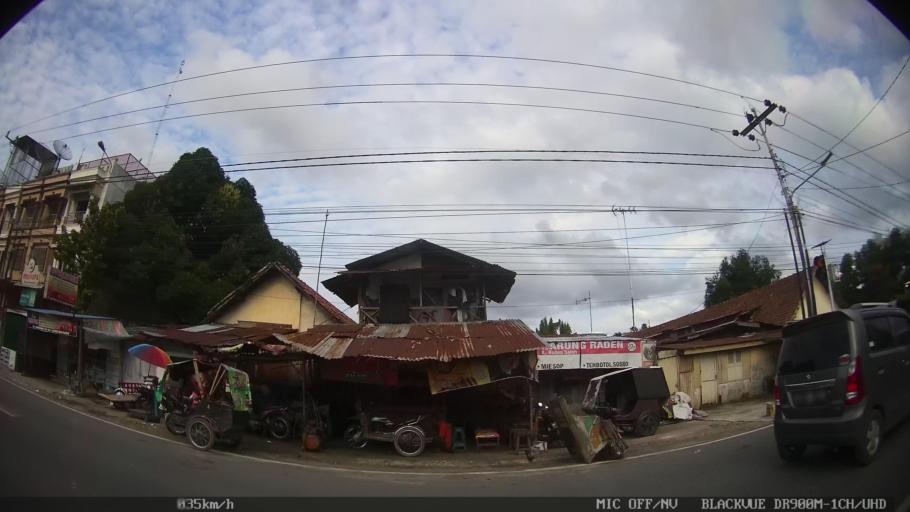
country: ID
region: North Sumatra
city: Medan
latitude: 3.6016
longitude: 98.6775
